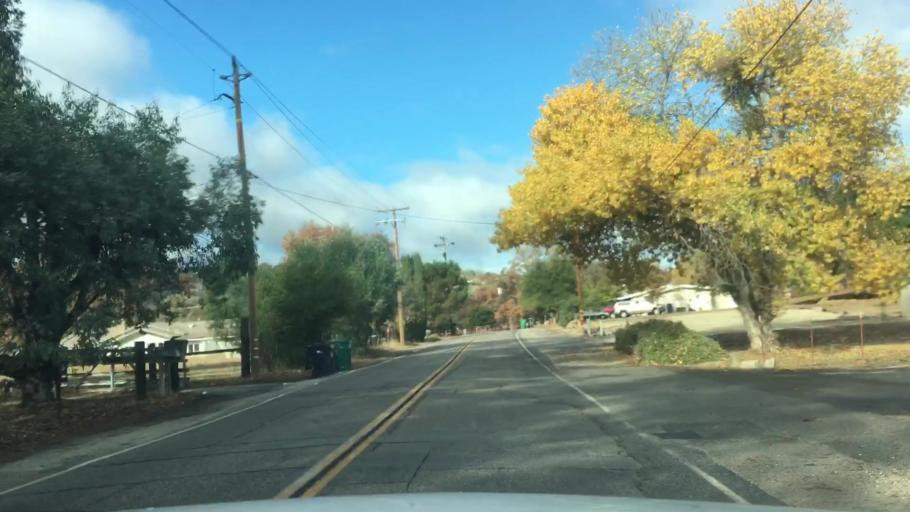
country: US
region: California
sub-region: San Luis Obispo County
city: Atascadero
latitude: 35.4607
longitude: -120.6723
